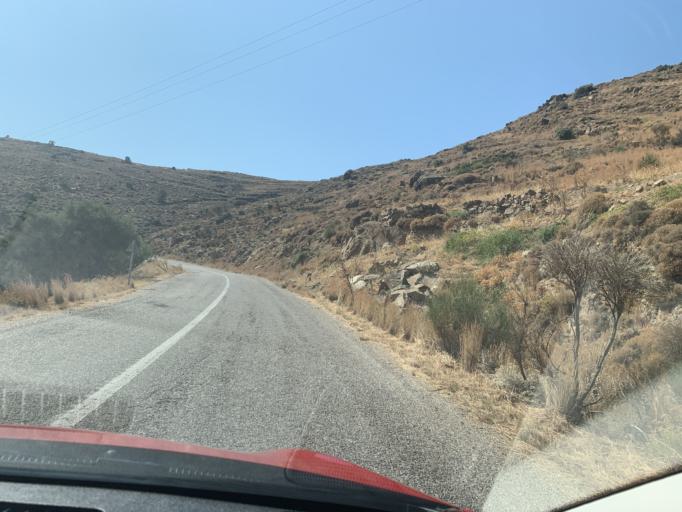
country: GR
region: North Aegean
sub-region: Chios
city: Vrontados
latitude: 38.4806
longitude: 25.8956
